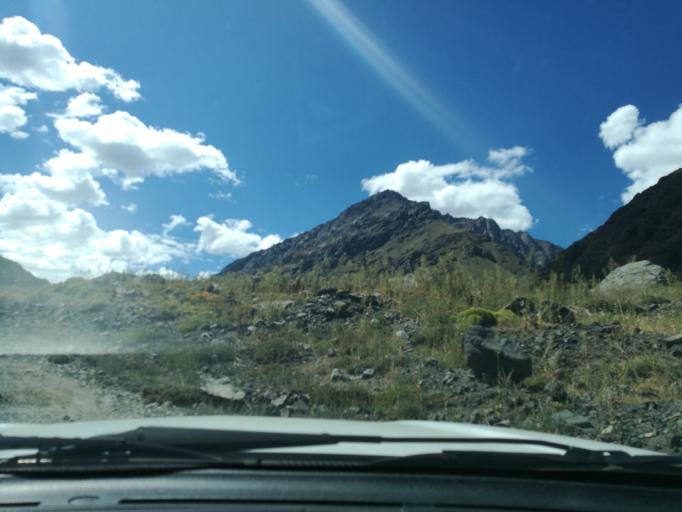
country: CL
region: O'Higgins
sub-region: Provincia de Cachapoal
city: Machali
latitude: -34.4101
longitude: -70.2358
